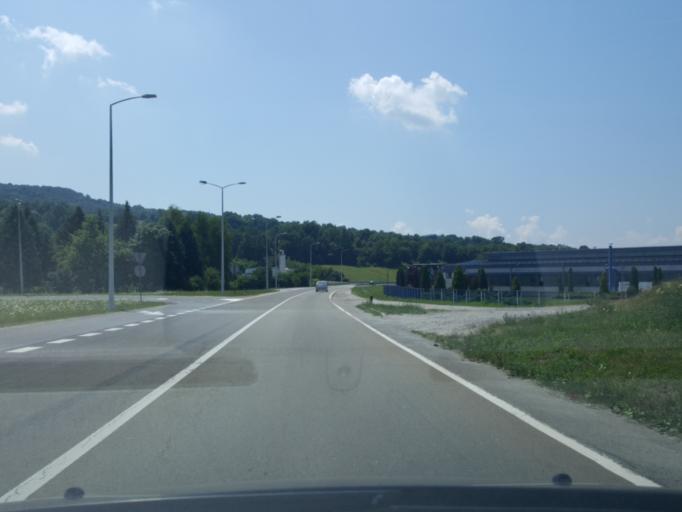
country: RS
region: Central Serbia
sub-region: Moravicki Okrug
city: Gornji Milanovac
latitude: 44.0395
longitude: 20.4848
